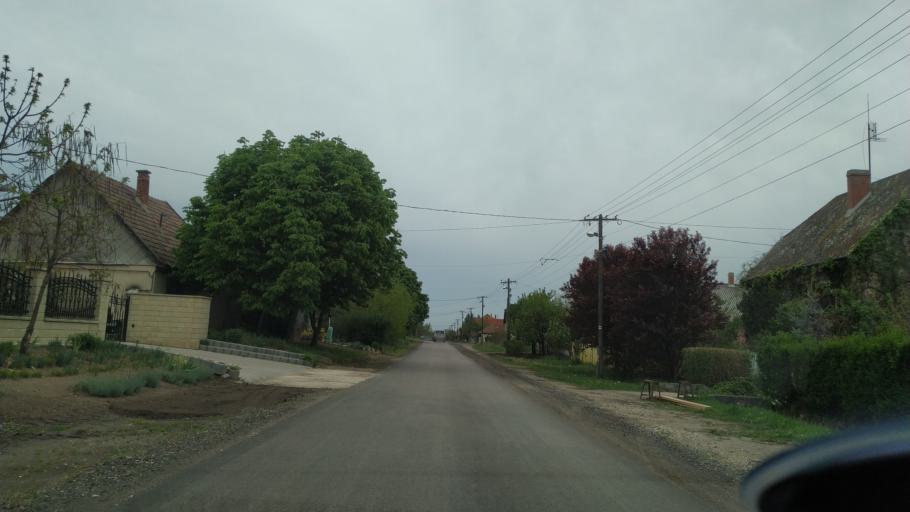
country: HU
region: Pest
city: Nagykata
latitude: 47.4213
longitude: 19.7202
